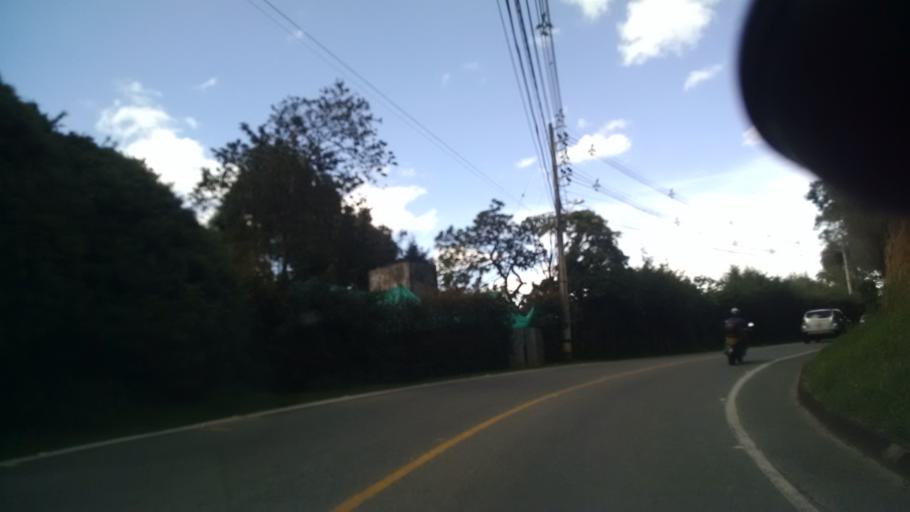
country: CO
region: Antioquia
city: El Retiro
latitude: 6.0759
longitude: -75.4974
